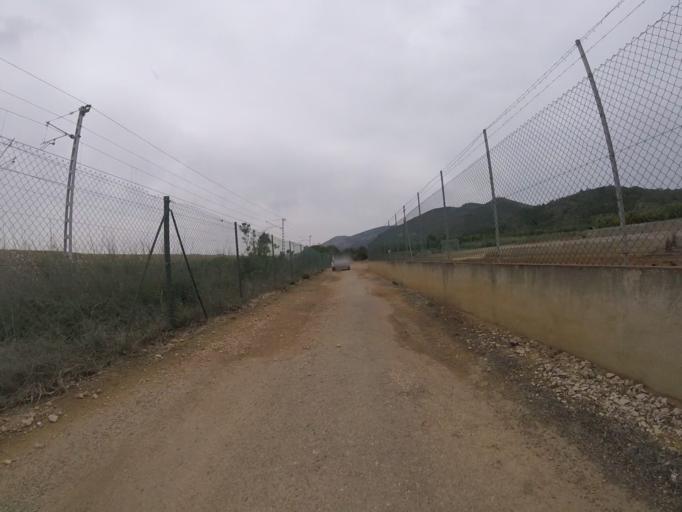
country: ES
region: Valencia
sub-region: Provincia de Castello
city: Alcoceber
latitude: 40.2552
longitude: 0.2524
